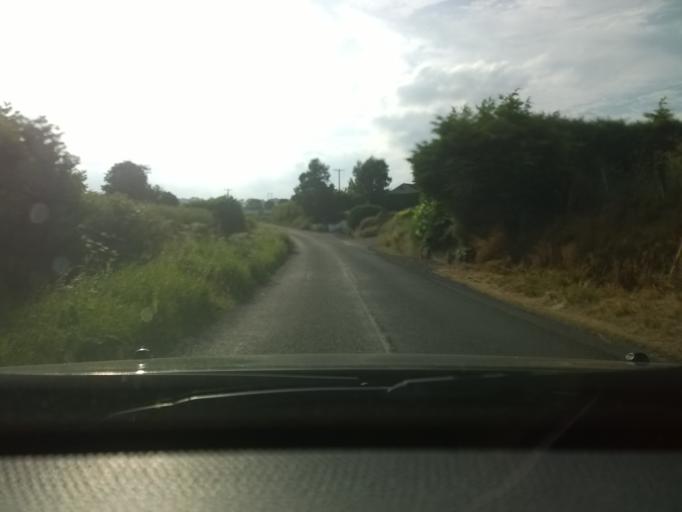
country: IE
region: Leinster
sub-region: Kildare
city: Kildare
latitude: 53.1773
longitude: -6.9216
